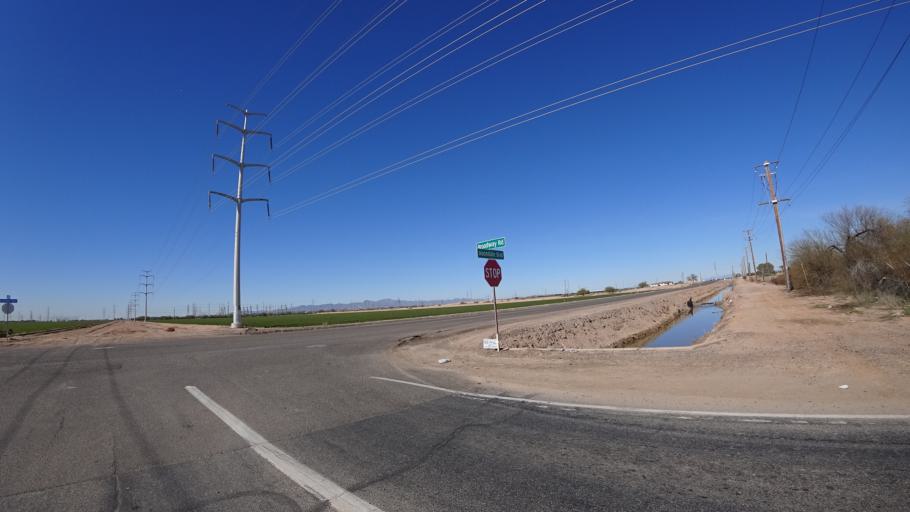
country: US
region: Arizona
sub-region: Maricopa County
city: Avondale
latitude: 33.4062
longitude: -112.3059
